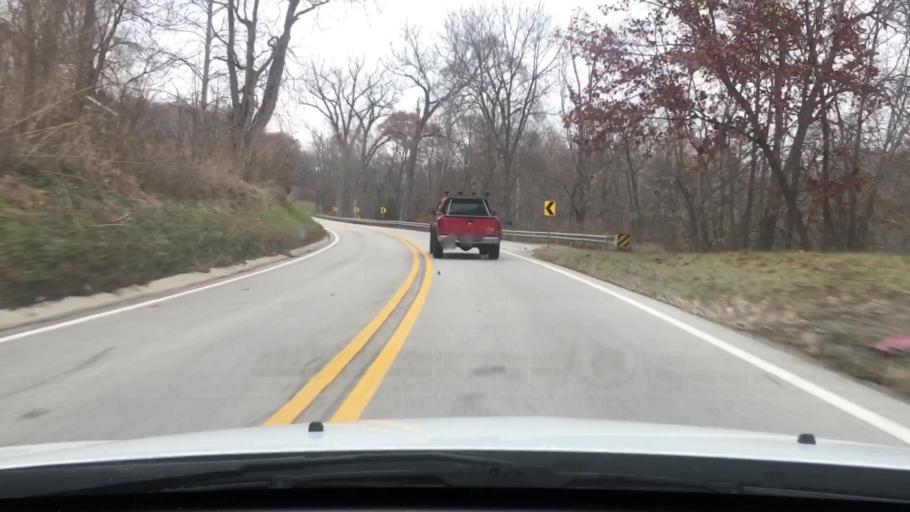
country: US
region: Missouri
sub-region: Pike County
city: Louisiana
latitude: 39.5196
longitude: -90.9491
